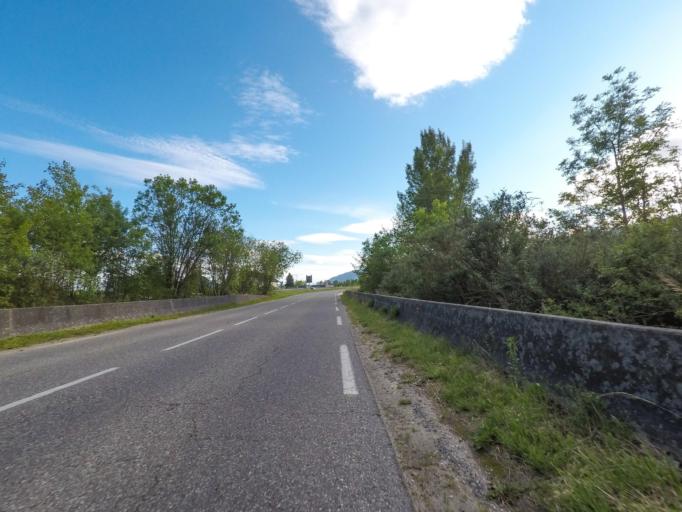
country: FR
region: Rhone-Alpes
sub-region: Departement de l'Ain
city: Thoiry
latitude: 46.2311
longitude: 5.9998
